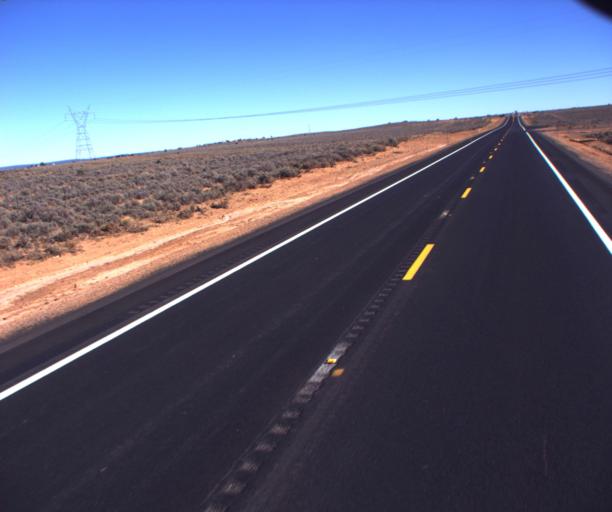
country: US
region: Arizona
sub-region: Apache County
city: Ganado
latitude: 35.7175
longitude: -109.4602
